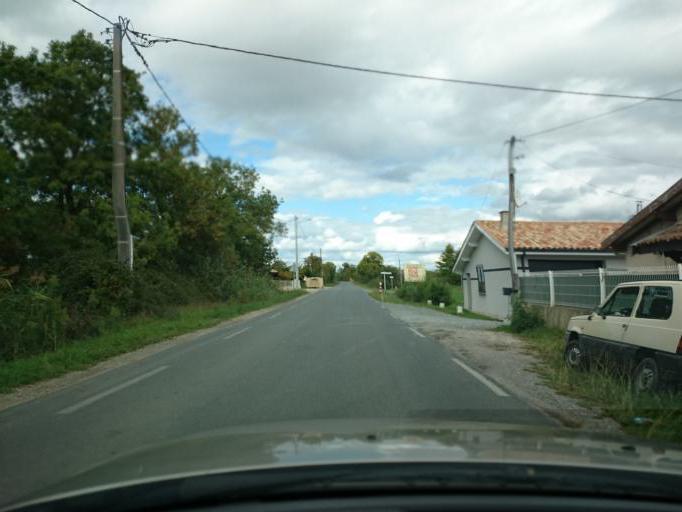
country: FR
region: Aquitaine
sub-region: Departement de la Gironde
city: Saint-Louis-de-Montferrand
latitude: 44.9538
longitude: -0.5525
